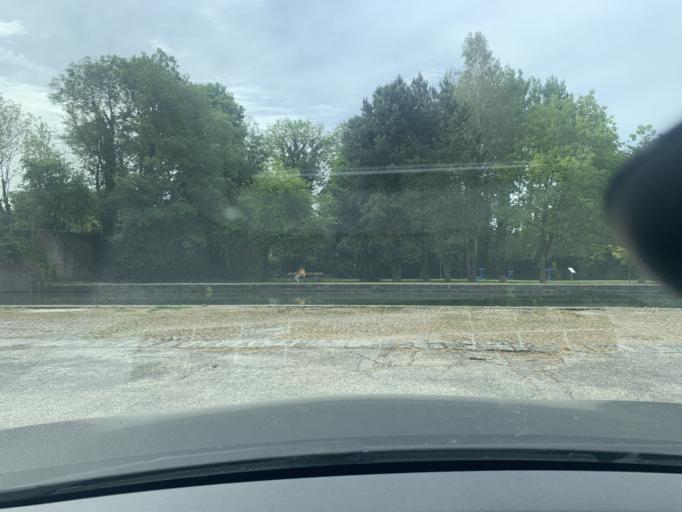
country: FR
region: Nord-Pas-de-Calais
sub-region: Departement du Nord
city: Marcoing
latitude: 50.1242
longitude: 3.1829
